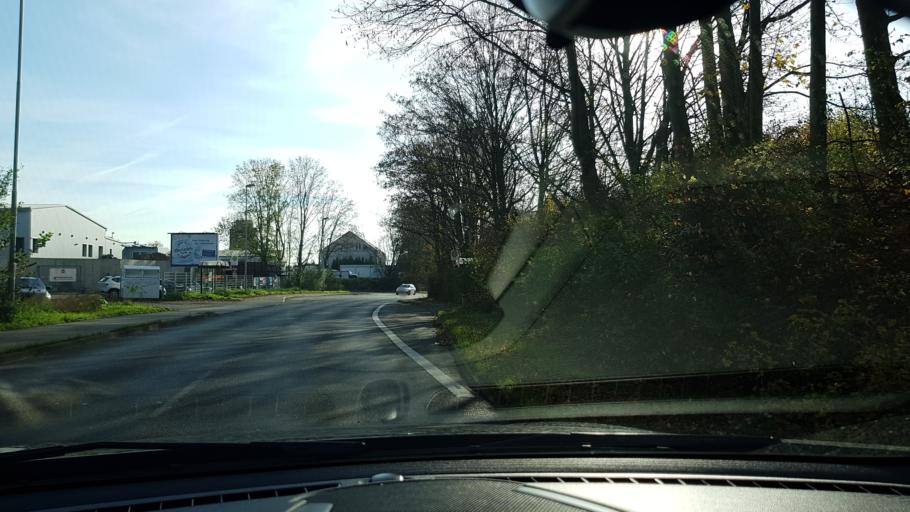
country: DE
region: North Rhine-Westphalia
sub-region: Regierungsbezirk Dusseldorf
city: Neubrueck
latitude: 51.1334
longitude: 6.6174
